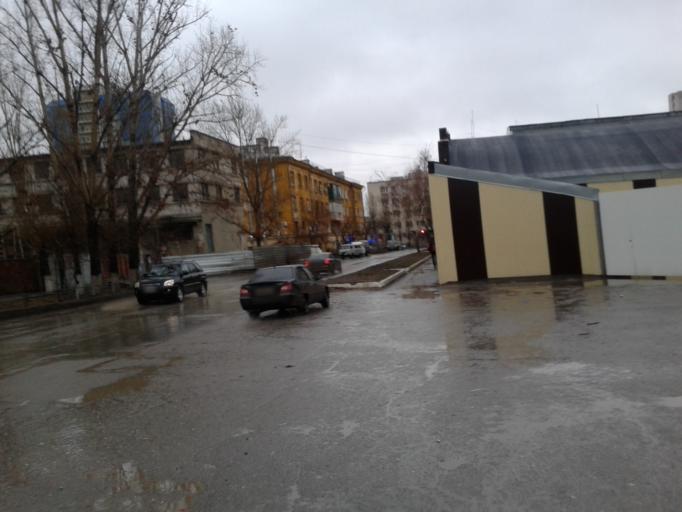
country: RU
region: Volgograd
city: Volgograd
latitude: 48.6949
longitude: 44.4872
